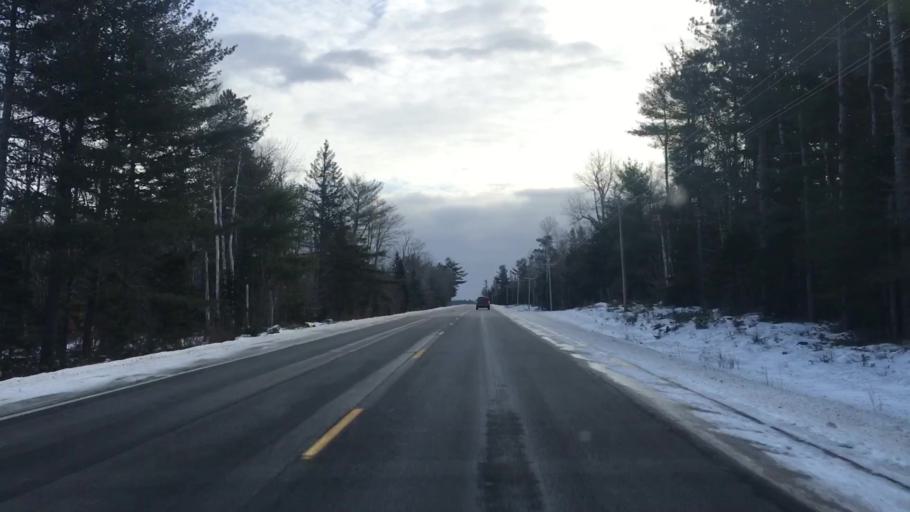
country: US
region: Maine
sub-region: Washington County
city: Machias
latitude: 44.9998
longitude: -67.5972
